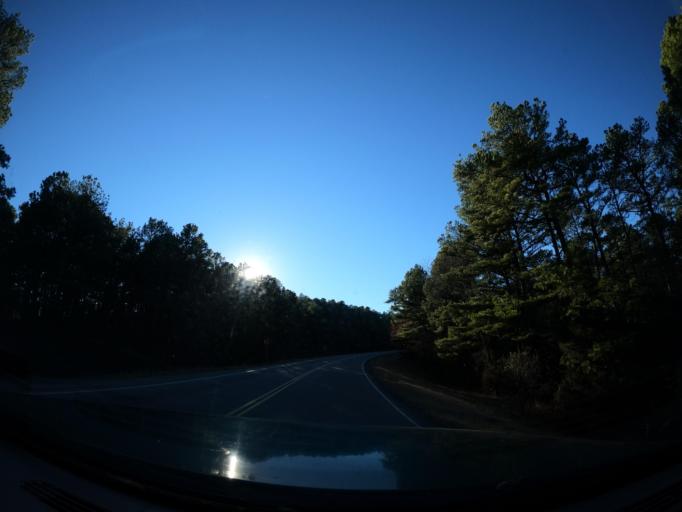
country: US
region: Oklahoma
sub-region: Latimer County
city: Wilburton
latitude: 35.0012
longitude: -95.3355
